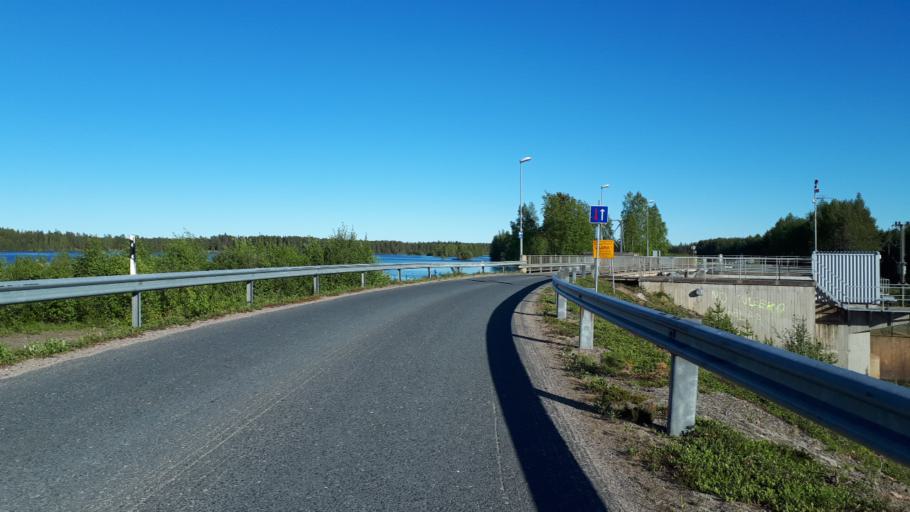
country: FI
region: Northern Ostrobothnia
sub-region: Oulunkaari
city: Ii
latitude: 65.3254
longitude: 25.5236
